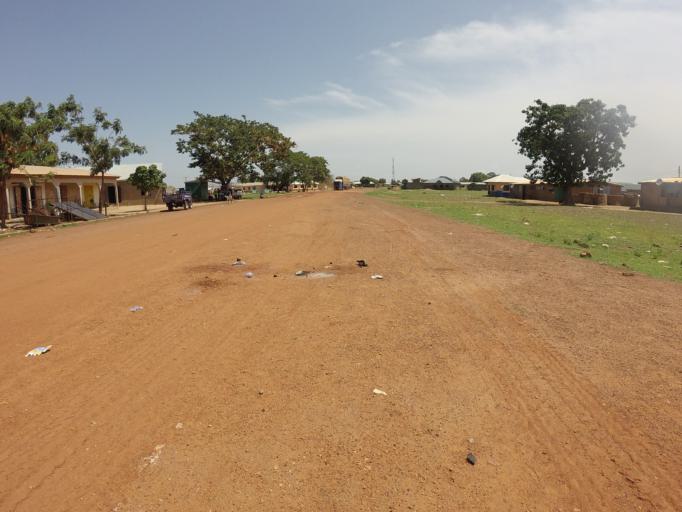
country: GH
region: Upper East
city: Bawku
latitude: 11.1511
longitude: -0.2061
